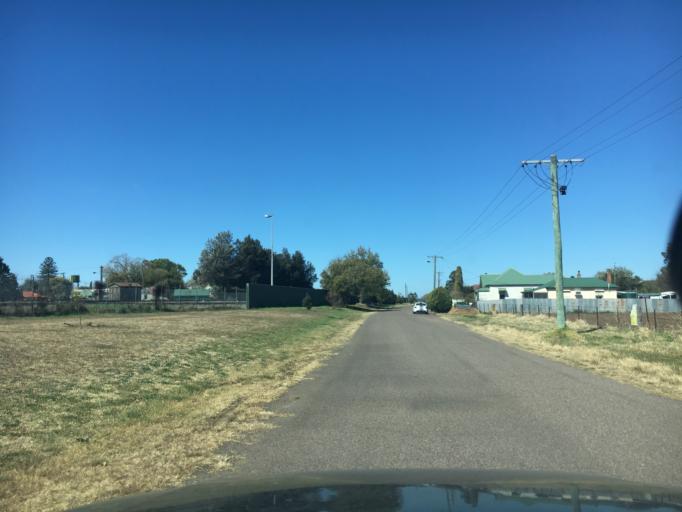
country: AU
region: New South Wales
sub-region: Singleton
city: Singleton
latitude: -32.5746
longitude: 151.1683
